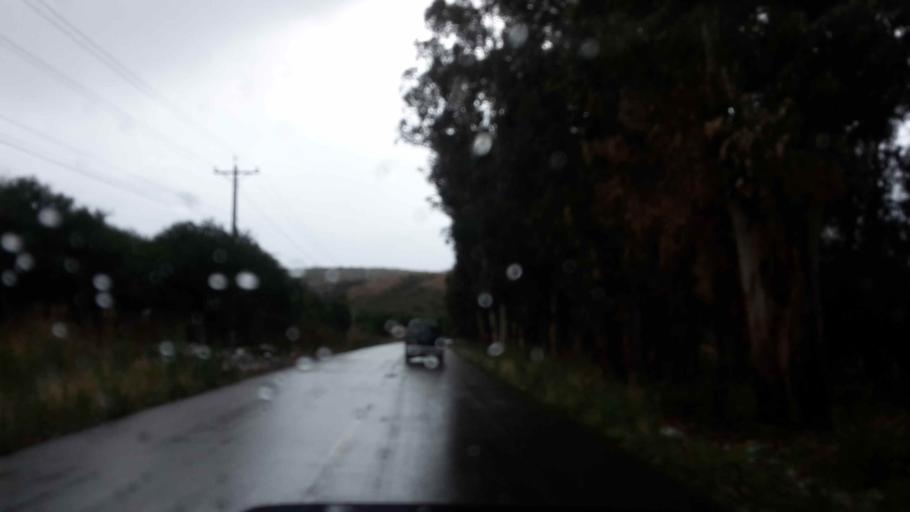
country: BO
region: Cochabamba
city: Tarata
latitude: -17.5401
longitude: -66.1145
